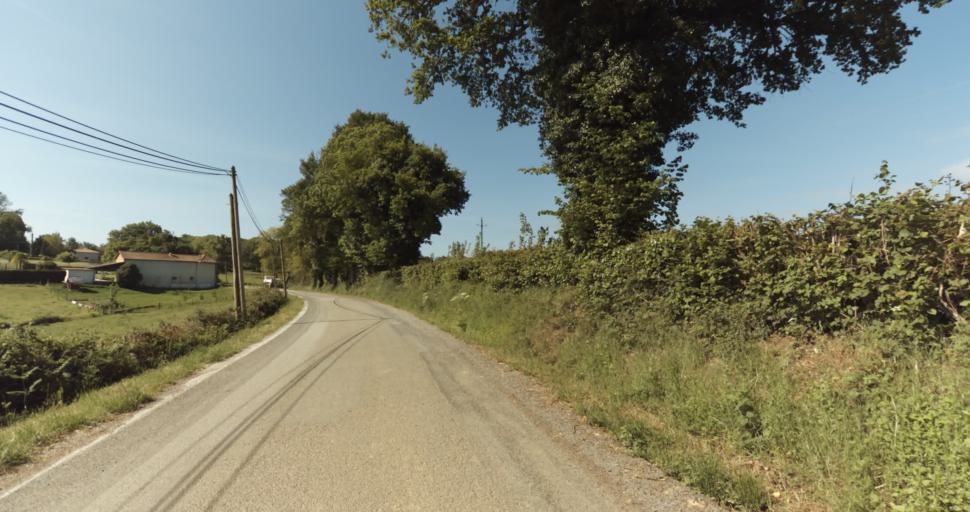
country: FR
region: Limousin
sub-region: Departement de la Haute-Vienne
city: Solignac
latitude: 45.7246
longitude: 1.2691
